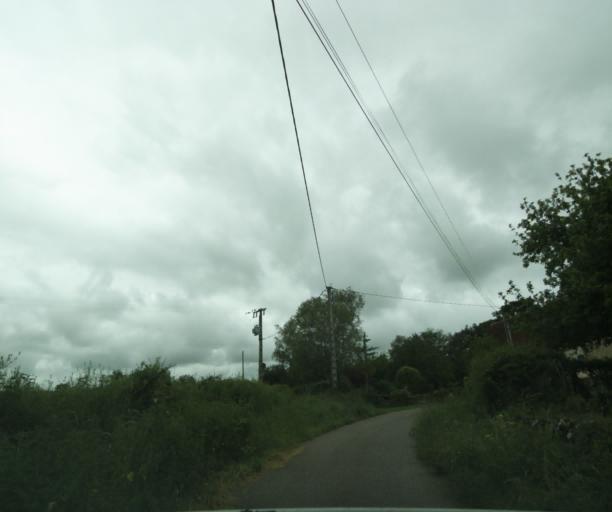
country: FR
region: Bourgogne
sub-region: Departement de Saone-et-Loire
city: Charolles
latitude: 46.4832
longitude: 4.3219
